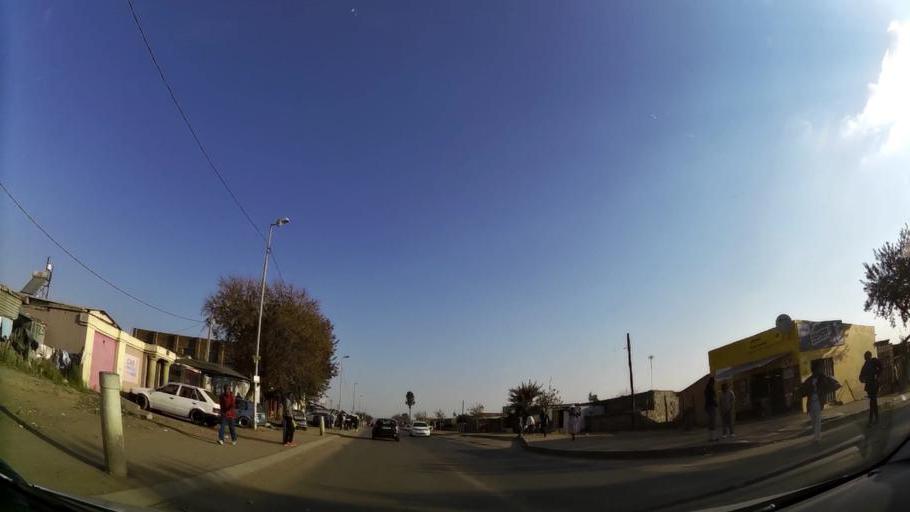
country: ZA
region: Gauteng
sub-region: Ekurhuleni Metropolitan Municipality
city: Tembisa
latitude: -25.9915
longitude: 28.2006
